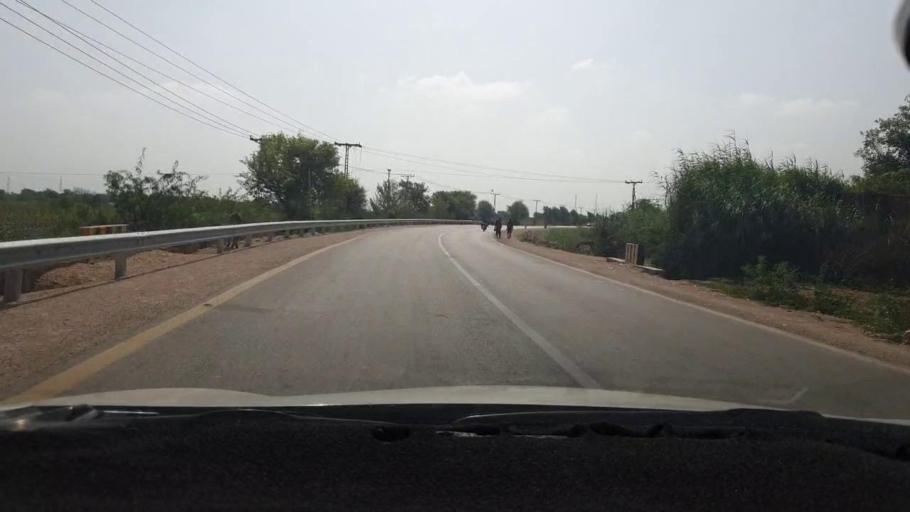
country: PK
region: Sindh
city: Mirpur Khas
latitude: 25.7197
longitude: 69.1190
